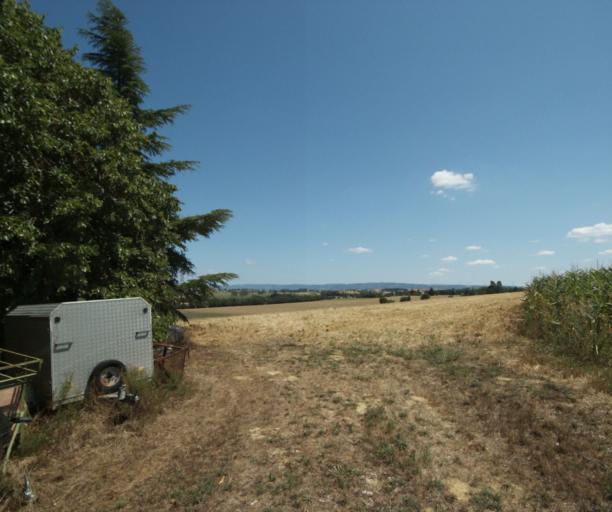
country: FR
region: Midi-Pyrenees
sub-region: Departement de la Haute-Garonne
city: Saint-Felix-Lauragais
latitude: 43.4812
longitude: 1.8730
